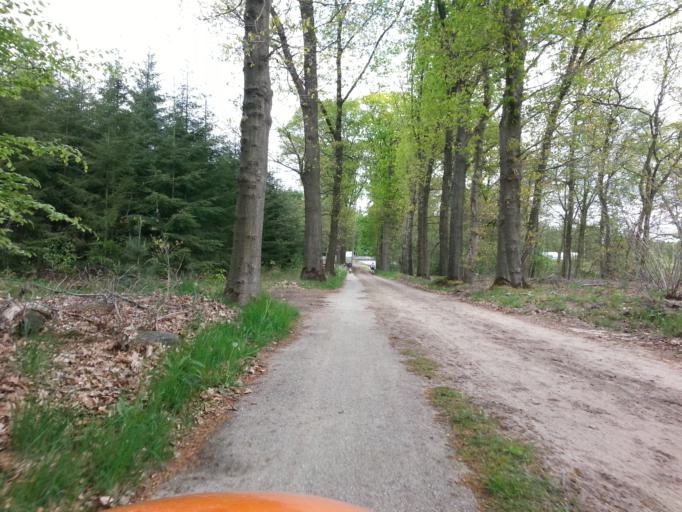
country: NL
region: Gelderland
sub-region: Gemeente Renkum
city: Wolfheze
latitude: 52.0200
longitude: 5.7702
